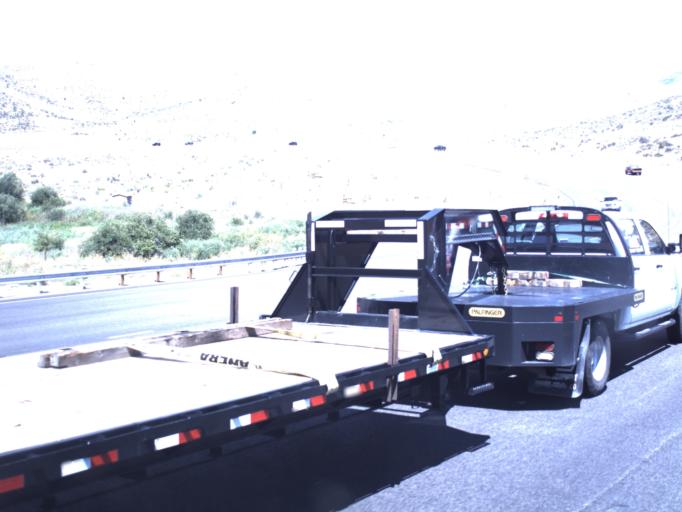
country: US
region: Utah
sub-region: Wasatch County
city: Midway
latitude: 40.4094
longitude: -111.4794
